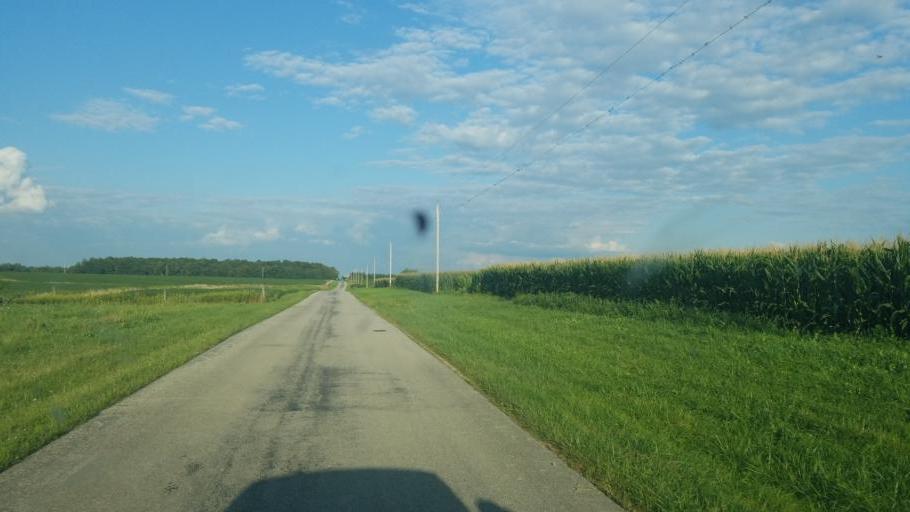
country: US
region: Ohio
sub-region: Huron County
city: Willard
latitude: 41.1098
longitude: -82.8494
